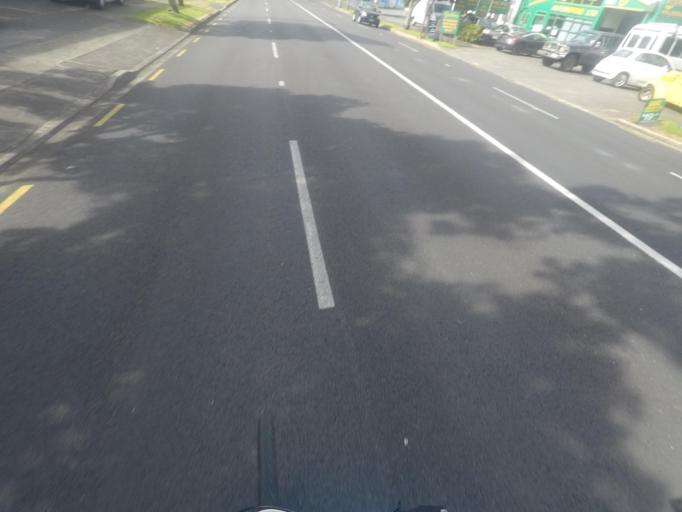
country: NZ
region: Auckland
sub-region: Auckland
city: Mangere
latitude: -36.9238
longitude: 174.7833
